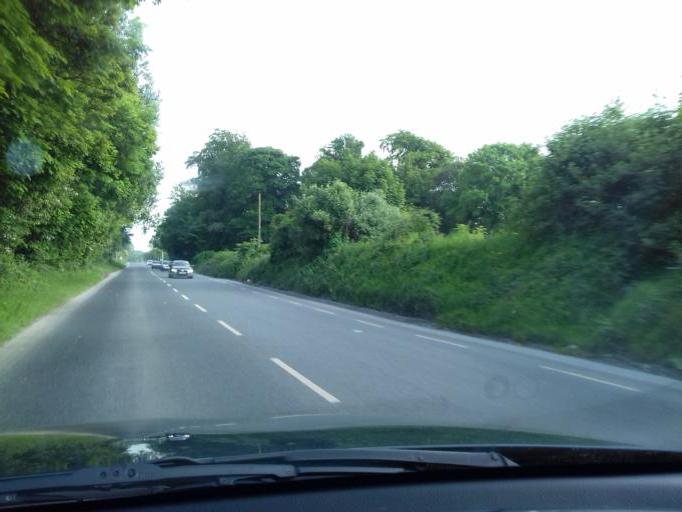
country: IE
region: Leinster
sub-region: Dublin City
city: Finglas
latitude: 53.4148
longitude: -6.3200
